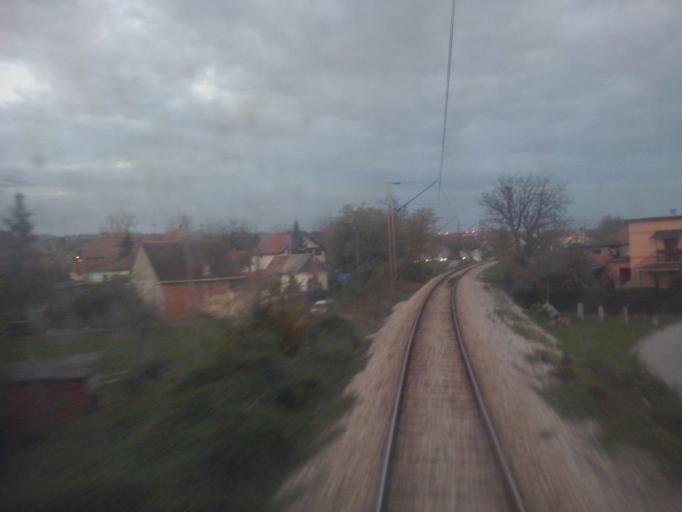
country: RS
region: Central Serbia
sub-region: Kolubarski Okrug
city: Valjevo
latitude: 44.2784
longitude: 19.9252
